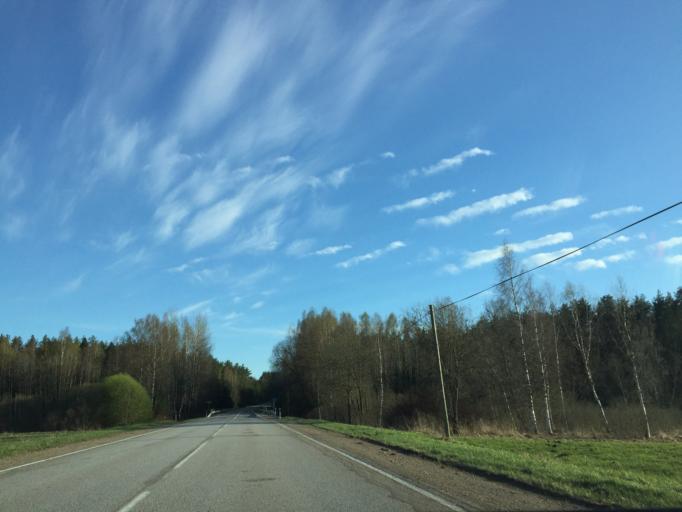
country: LV
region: Valkas Rajons
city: Valka
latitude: 57.7393
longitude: 25.9453
